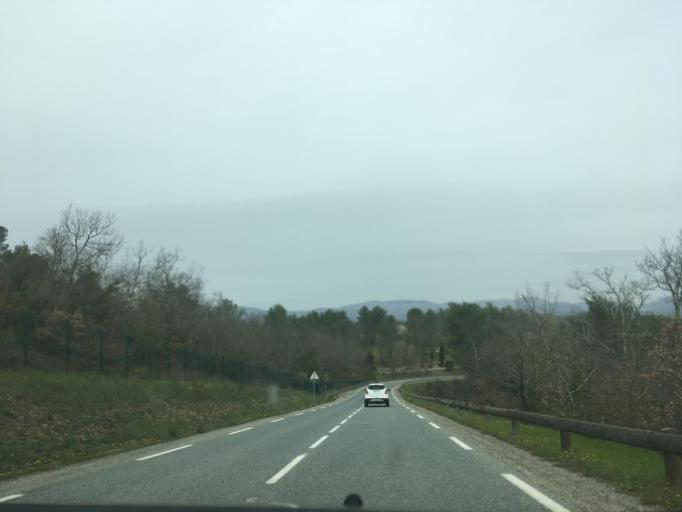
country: FR
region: Provence-Alpes-Cote d'Azur
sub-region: Departement du Var
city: Callian
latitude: 43.5929
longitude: 6.7422
